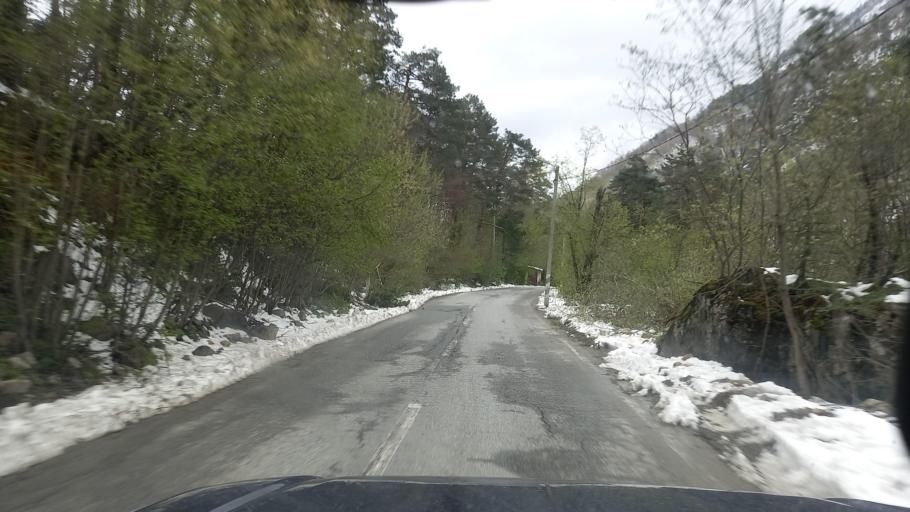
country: RU
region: North Ossetia
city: Mizur
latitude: 42.7929
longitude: 43.9201
